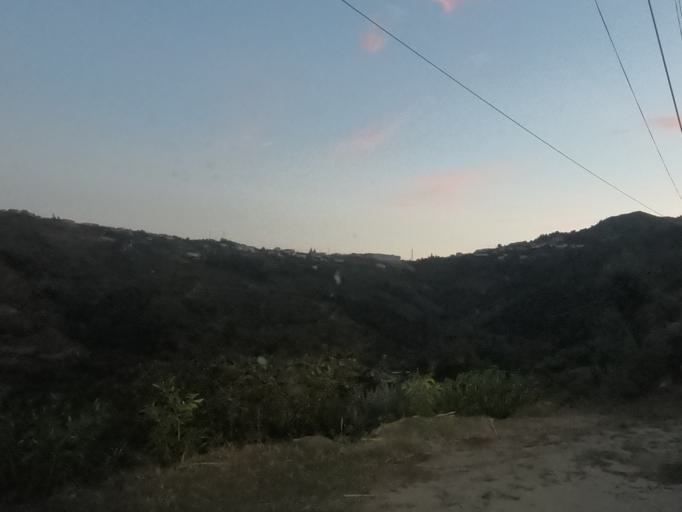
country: PT
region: Vila Real
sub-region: Vila Real
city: Vila Real
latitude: 41.2711
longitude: -7.7636
